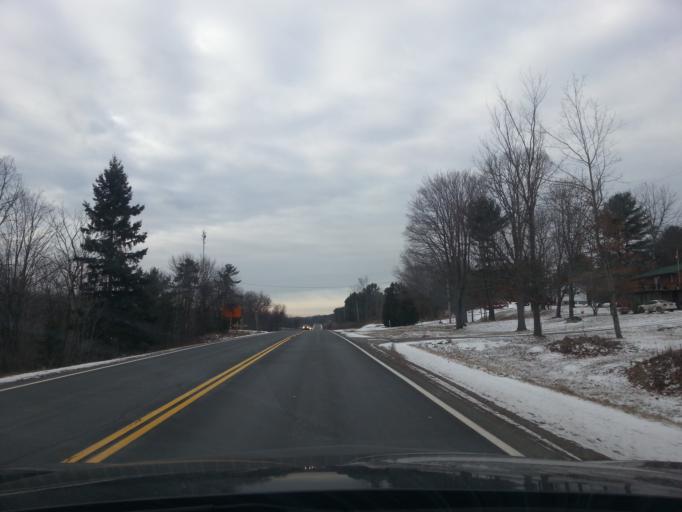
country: CA
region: Ontario
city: Greater Napanee
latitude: 44.6409
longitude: -77.1317
